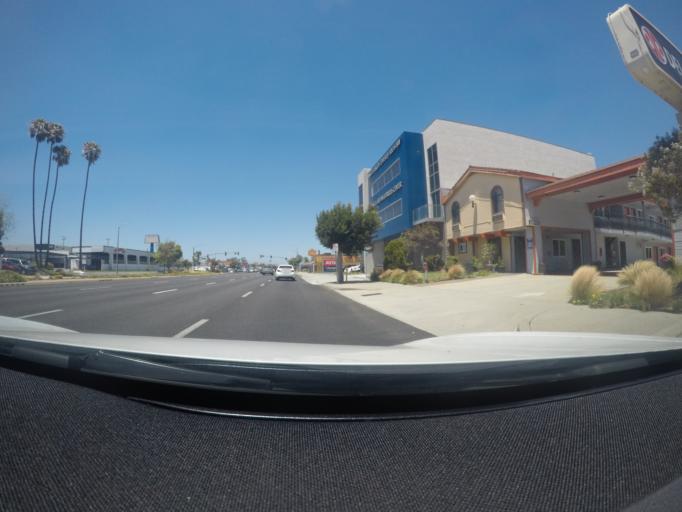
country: US
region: California
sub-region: Los Angeles County
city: Torrance
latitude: 33.8439
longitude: -118.3536
